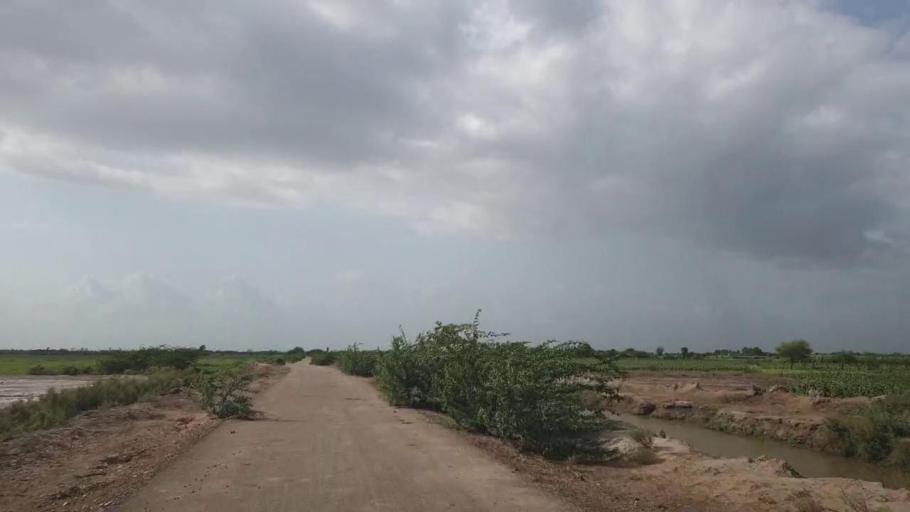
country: PK
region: Sindh
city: Kadhan
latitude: 24.5714
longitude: 69.0615
